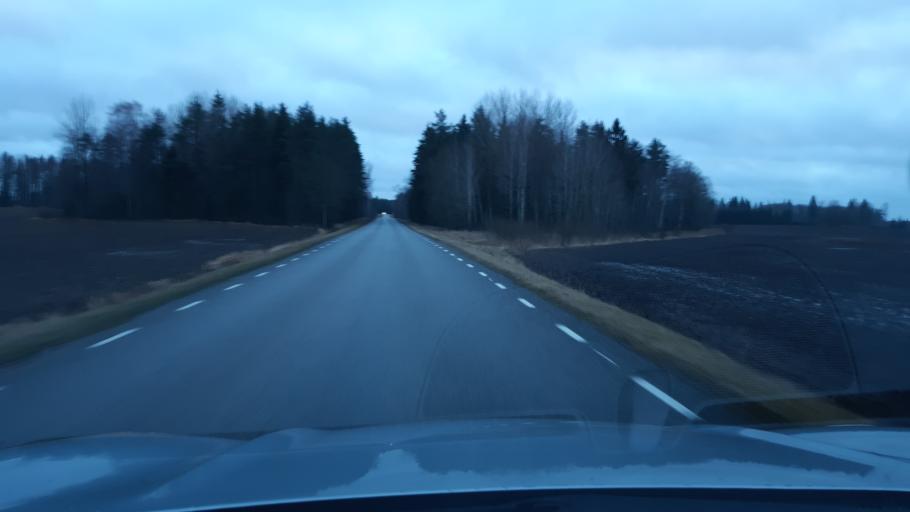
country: EE
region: Raplamaa
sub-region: Rapla vald
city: Rapla
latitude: 59.0317
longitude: 24.6783
